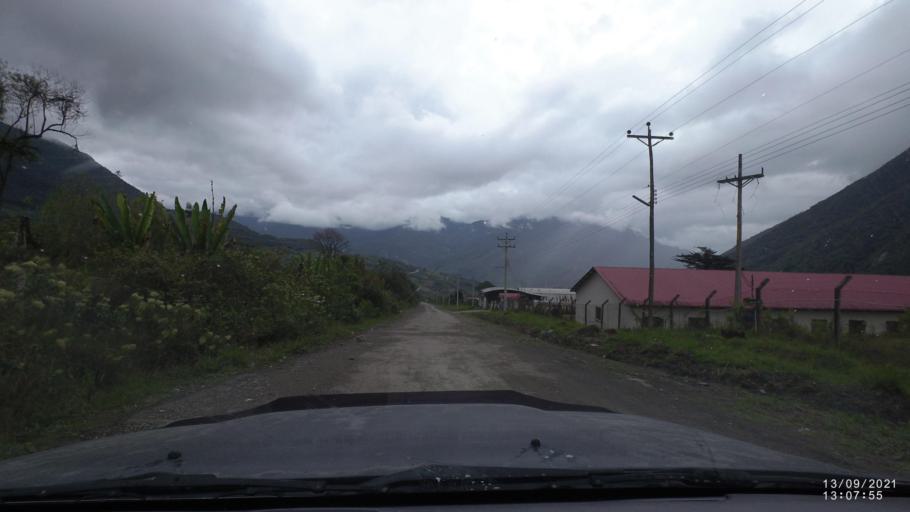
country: BO
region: Cochabamba
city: Colomi
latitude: -17.2186
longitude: -65.8228
